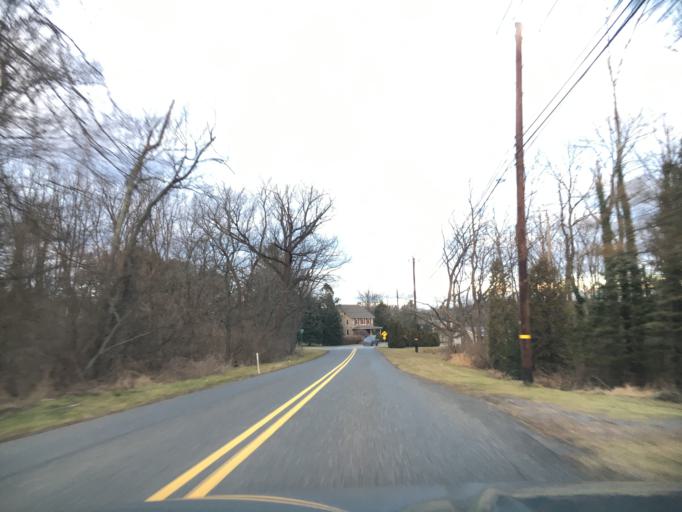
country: US
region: Pennsylvania
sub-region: Lehigh County
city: Schnecksville
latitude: 40.6924
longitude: -75.6070
